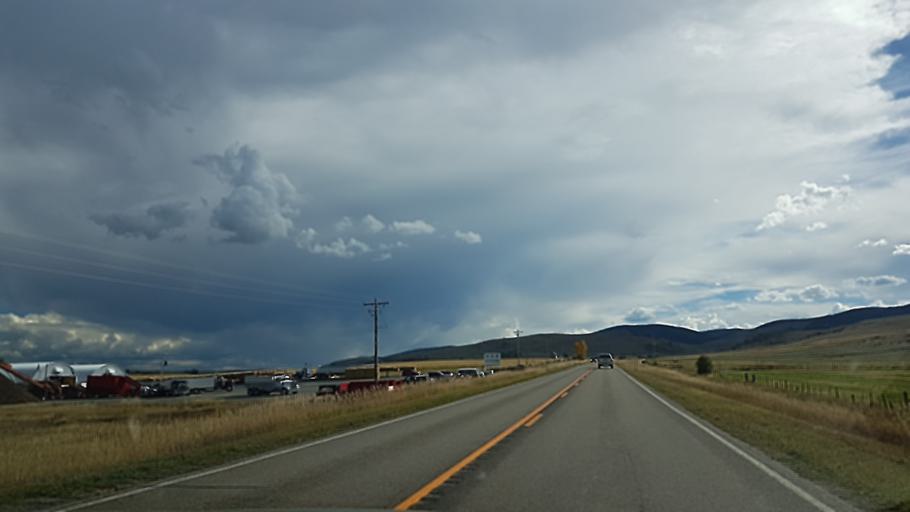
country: US
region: Montana
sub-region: Jefferson County
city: Whitehall
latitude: 45.7956
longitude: -111.9196
